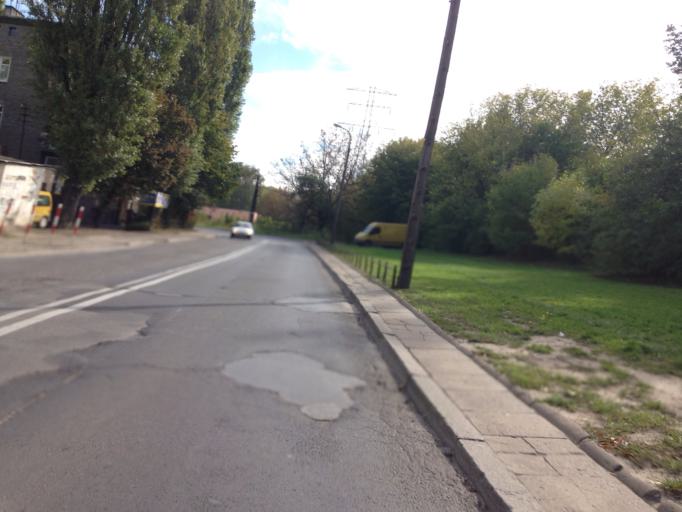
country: PL
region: Masovian Voivodeship
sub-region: Warszawa
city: Praga Polnoc
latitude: 52.2624
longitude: 21.0607
